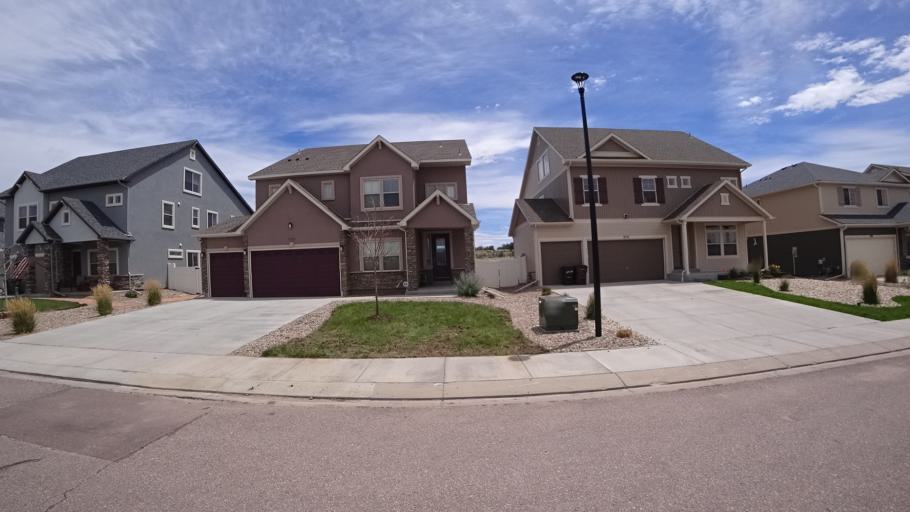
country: US
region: Colorado
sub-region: El Paso County
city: Fountain
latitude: 38.6949
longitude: -104.6788
